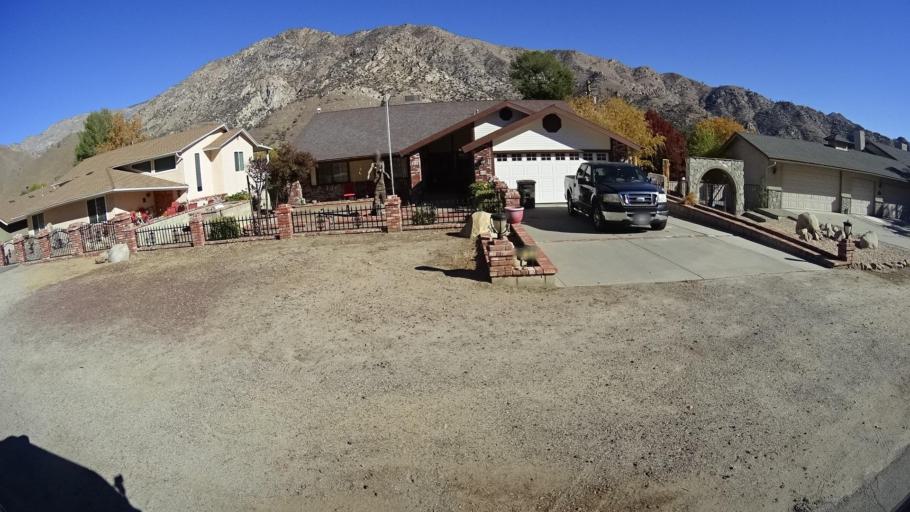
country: US
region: California
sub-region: Kern County
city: Kernville
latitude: 35.7634
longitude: -118.4314
